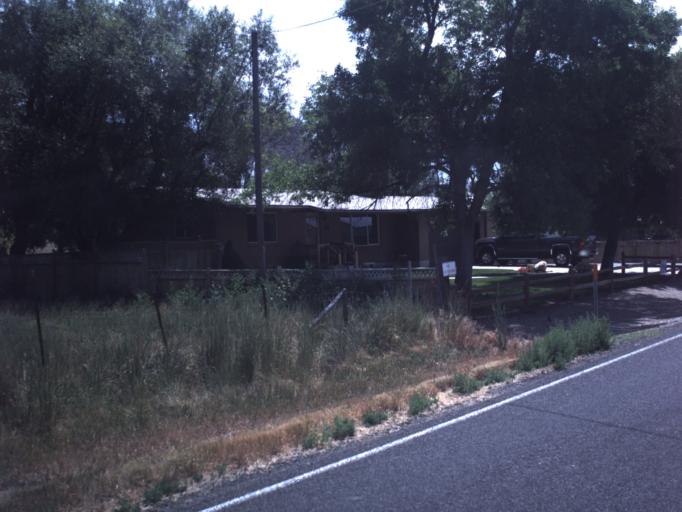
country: US
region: Utah
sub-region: Box Elder County
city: Tremonton
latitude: 41.6522
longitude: -112.2957
